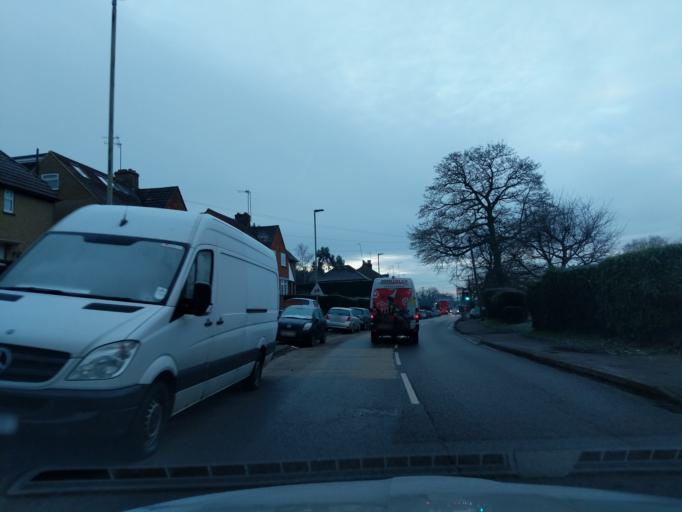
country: GB
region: England
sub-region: Hertfordshire
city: Kings Langley
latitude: 51.7171
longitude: -0.4430
